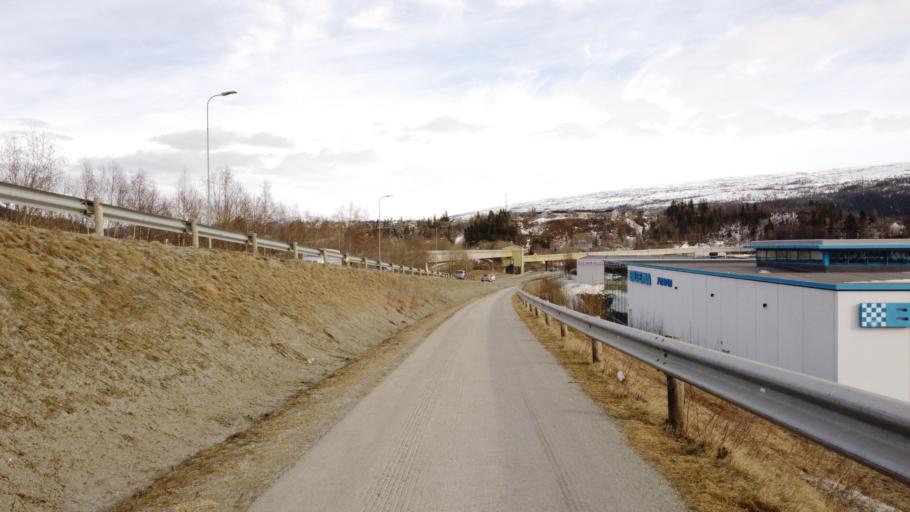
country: NO
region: Nordland
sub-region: Rana
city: Mo i Rana
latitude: 66.3234
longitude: 14.1639
